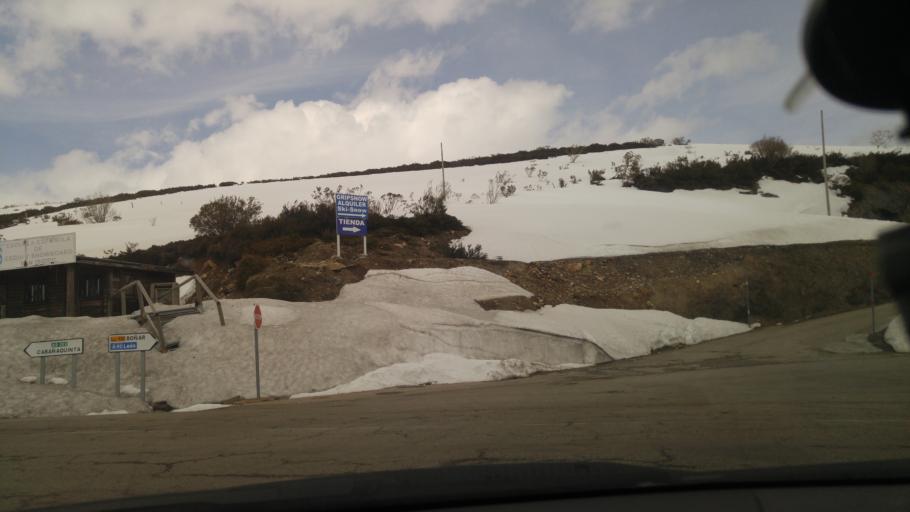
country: ES
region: Castille and Leon
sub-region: Provincia de Leon
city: Puebla de Lillo
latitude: 43.0638
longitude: -5.3772
